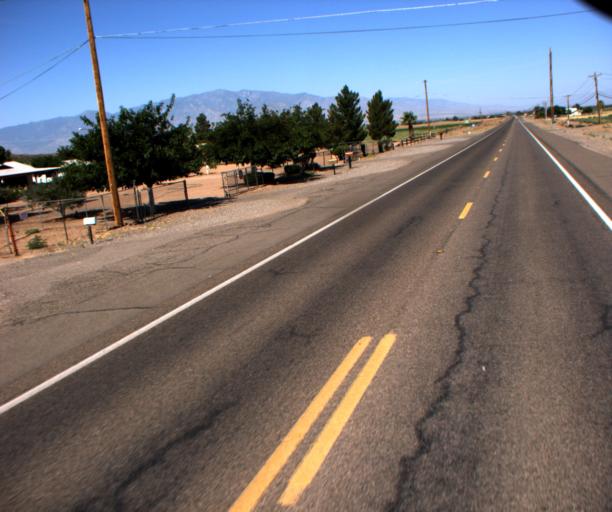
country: US
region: Arizona
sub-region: Graham County
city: Safford
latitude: 32.8128
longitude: -109.6022
